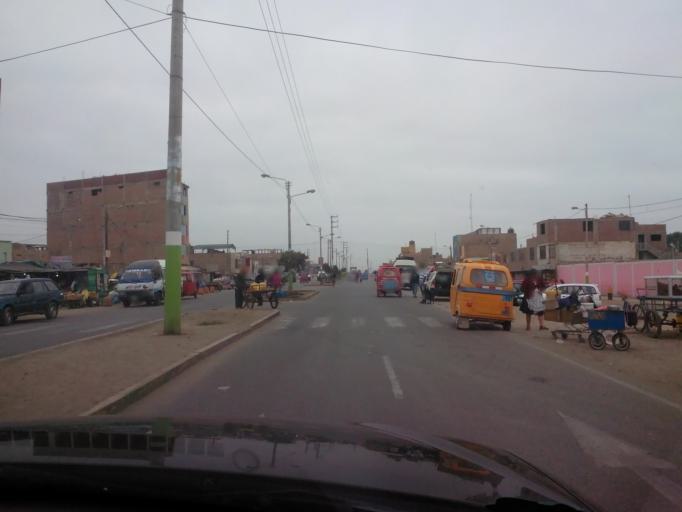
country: PE
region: Ica
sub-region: Provincia de Pisco
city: San Clemente
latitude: -13.6817
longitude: -76.1553
